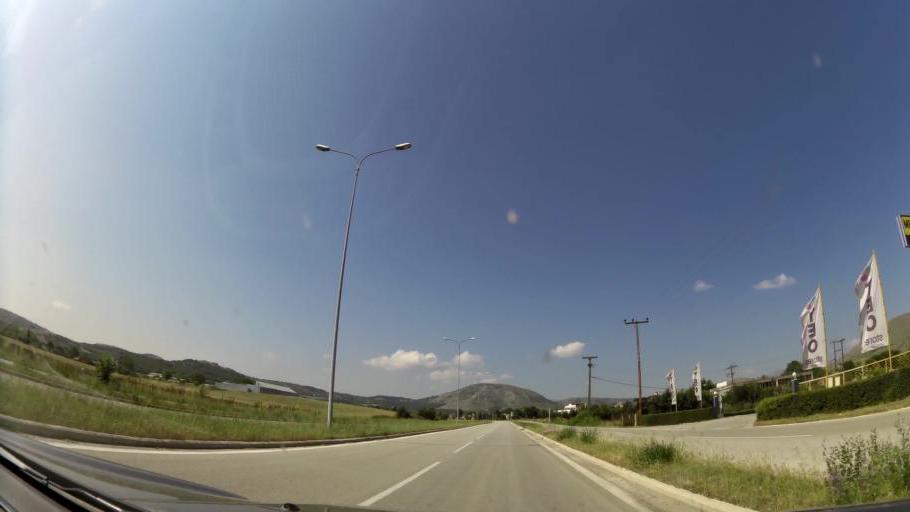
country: GR
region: West Macedonia
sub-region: Nomos Kozanis
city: Koila
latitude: 40.3424
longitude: 21.7955
